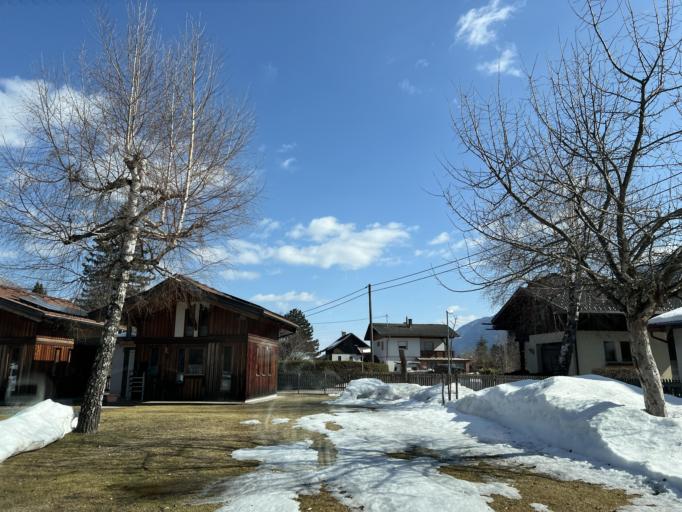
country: AT
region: Carinthia
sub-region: Politischer Bezirk Spittal an der Drau
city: Oberdrauburg
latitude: 46.6691
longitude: 12.9909
